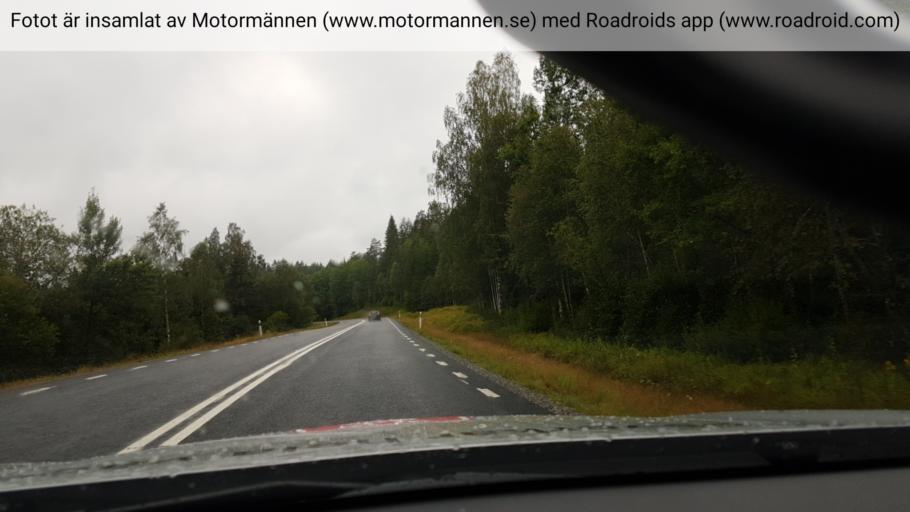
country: SE
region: Vaestra Goetaland
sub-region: Dals-Ed Kommun
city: Ed
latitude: 58.9090
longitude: 12.0046
